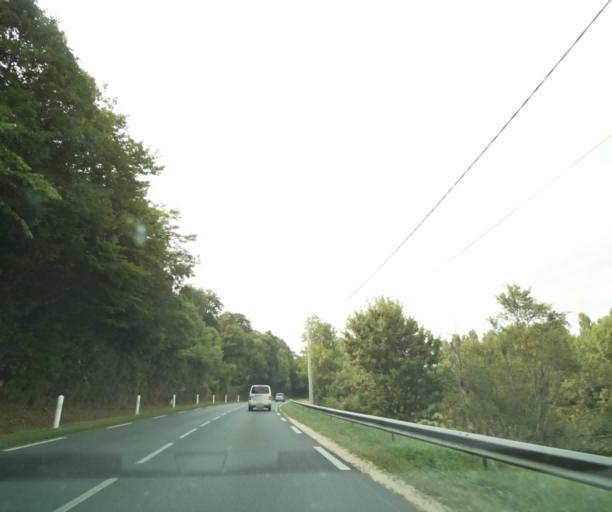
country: FR
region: Centre
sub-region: Departement de l'Indre
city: Clion
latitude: 46.9628
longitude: 1.2074
